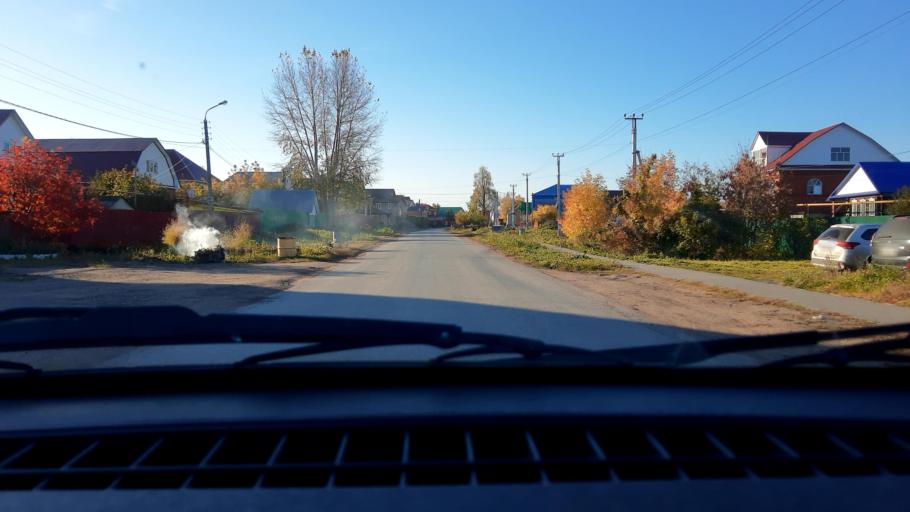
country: RU
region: Bashkortostan
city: Ufa
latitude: 54.6976
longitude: 55.9543
